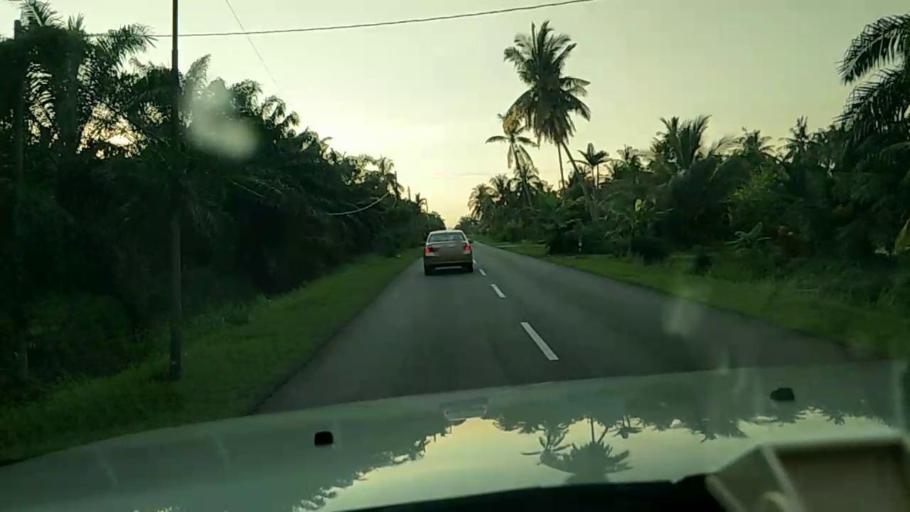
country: MY
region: Selangor
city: Kuala Selangor
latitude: 3.3144
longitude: 101.2838
